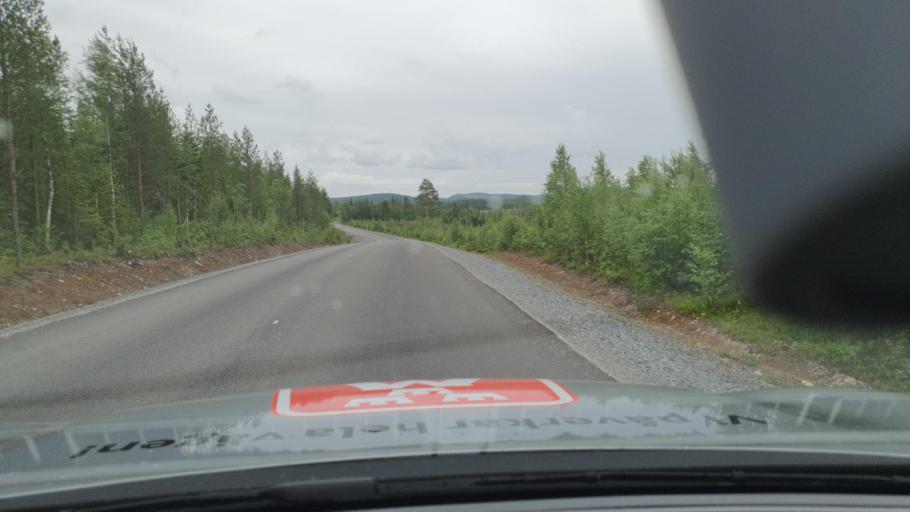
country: SE
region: Norrbotten
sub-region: Overtornea Kommun
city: OEvertornea
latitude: 66.5911
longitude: 23.3166
